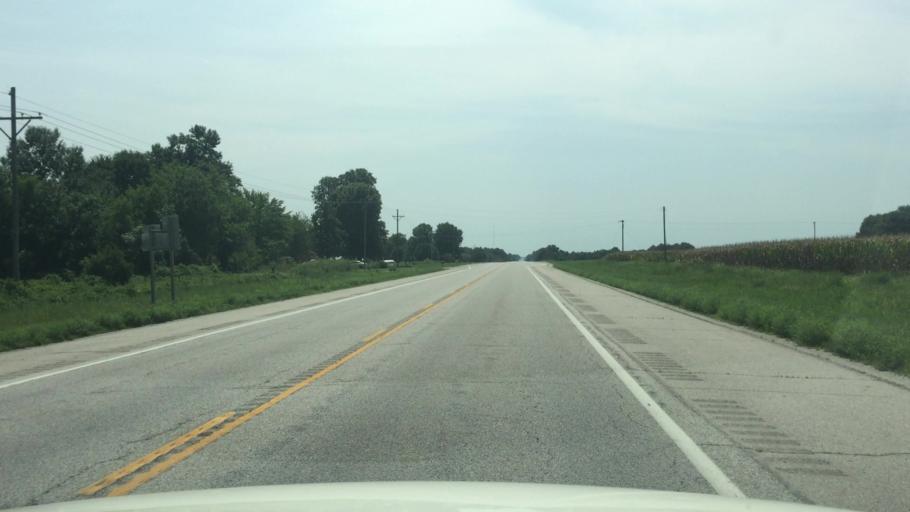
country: US
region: Kansas
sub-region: Cherokee County
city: Galena
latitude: 37.1509
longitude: -94.7043
